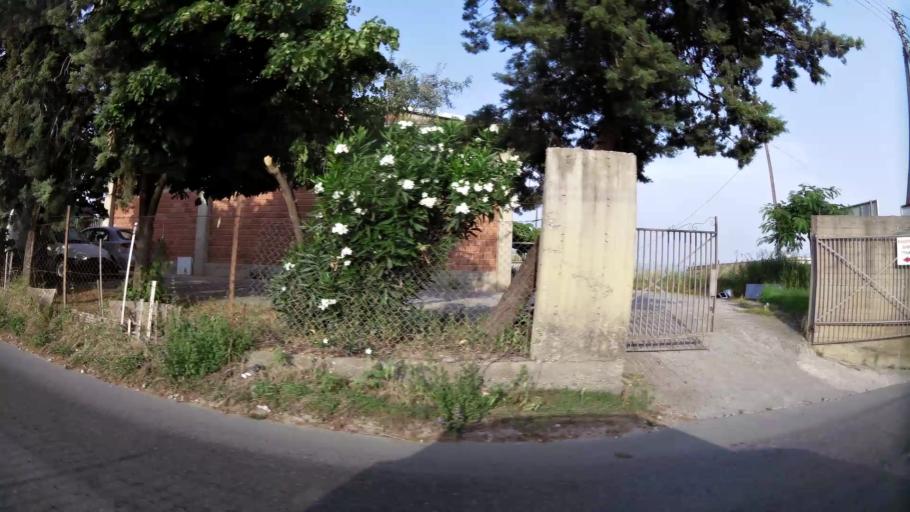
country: GR
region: Central Macedonia
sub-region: Nomos Thessalonikis
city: Evosmos
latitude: 40.6852
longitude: 22.9060
